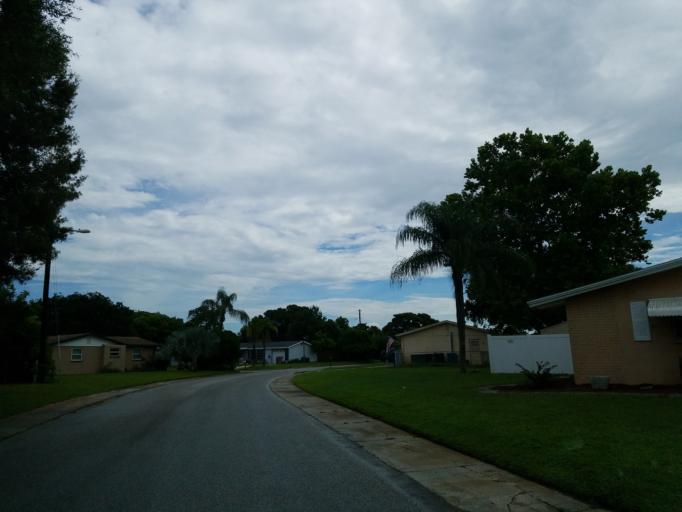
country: US
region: Florida
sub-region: Pasco County
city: Beacon Square
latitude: 28.2058
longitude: -82.7572
